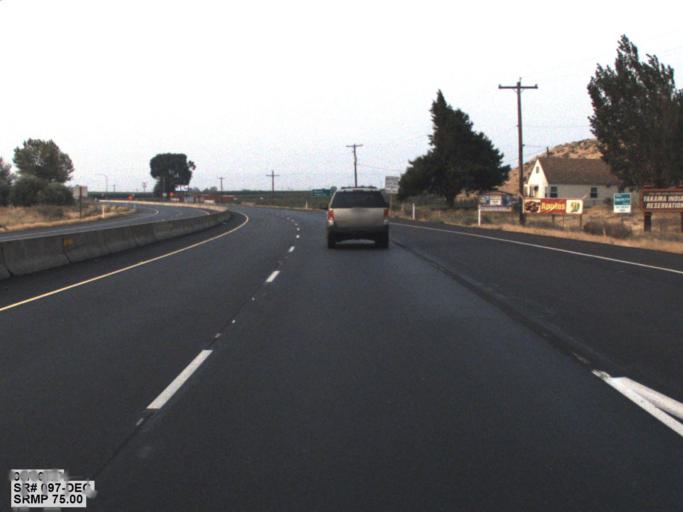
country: US
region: Washington
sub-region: Yakima County
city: Union Gap
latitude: 46.5235
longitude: -120.4796
